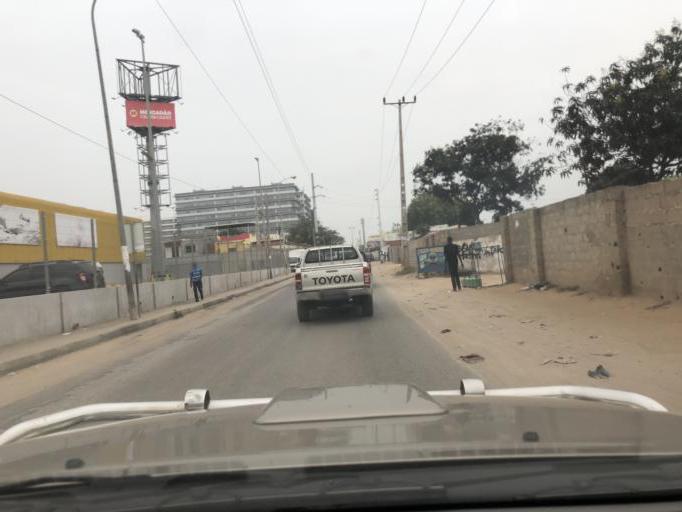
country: AO
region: Luanda
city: Luanda
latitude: -8.8861
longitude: 13.1843
